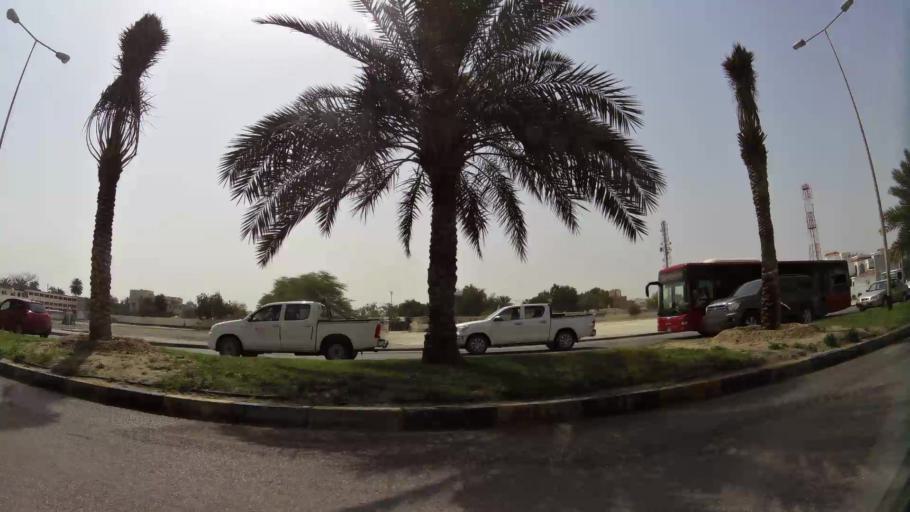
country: BH
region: Manama
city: Jidd Hafs
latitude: 26.2206
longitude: 50.5047
